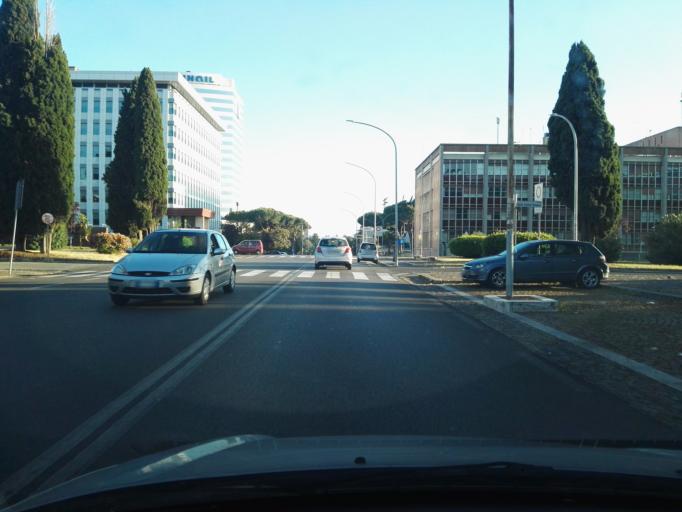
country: IT
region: Latium
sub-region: Citta metropolitana di Roma Capitale
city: Selcetta
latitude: 41.8326
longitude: 12.4759
